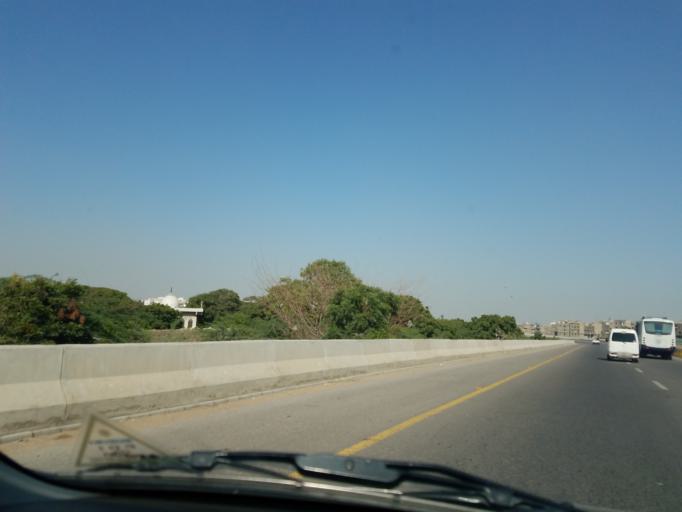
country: PK
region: Sindh
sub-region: Karachi District
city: Karachi
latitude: 24.9131
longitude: 67.0744
